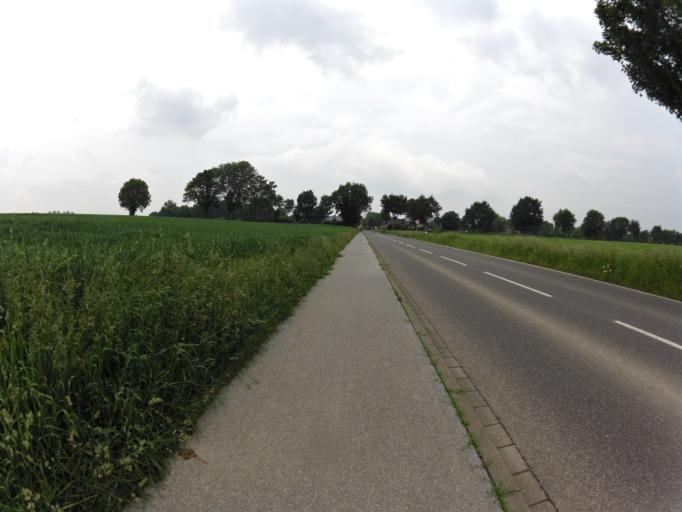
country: DE
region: North Rhine-Westphalia
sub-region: Regierungsbezirk Koln
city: Ubach-Palenberg
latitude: 50.9412
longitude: 6.1576
